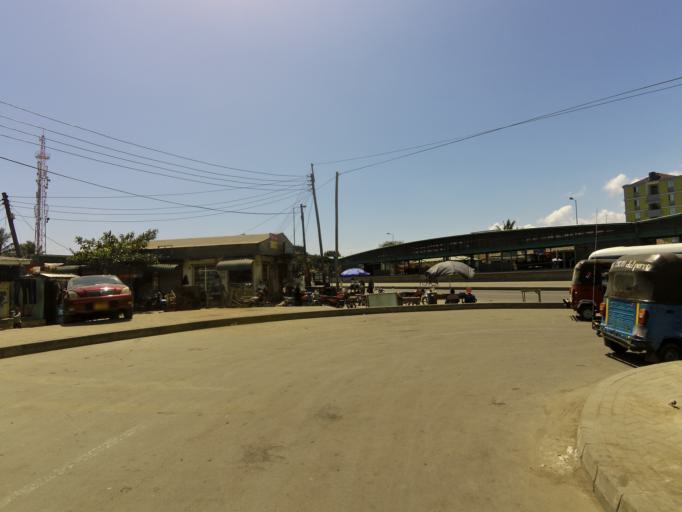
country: TZ
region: Dar es Salaam
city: Magomeni
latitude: -6.8039
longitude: 39.2601
